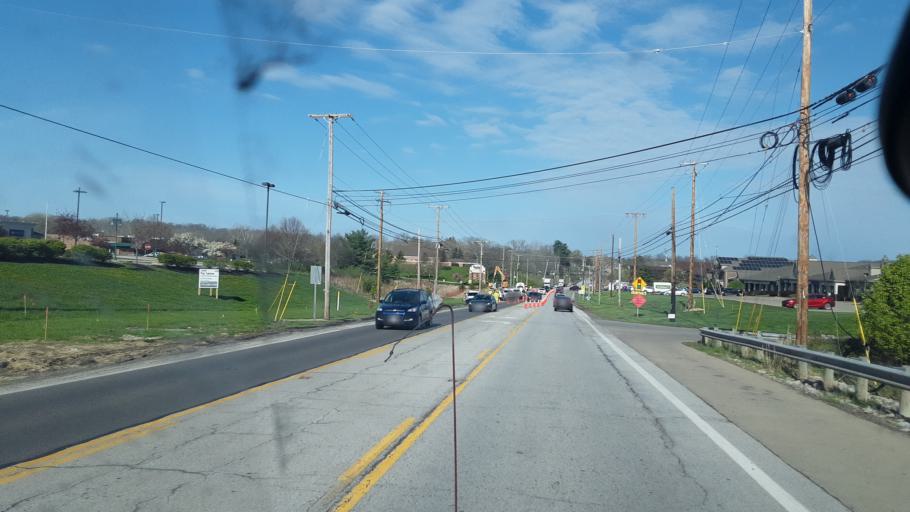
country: US
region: Ohio
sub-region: Medina County
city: Medina
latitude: 41.1364
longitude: -81.8140
